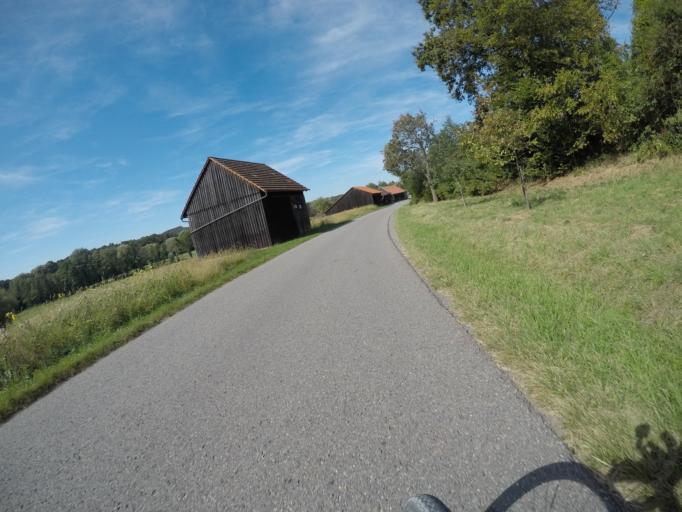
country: DE
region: Baden-Wuerttemberg
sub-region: Karlsruhe Region
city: Sternenfels
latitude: 49.0222
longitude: 8.8588
